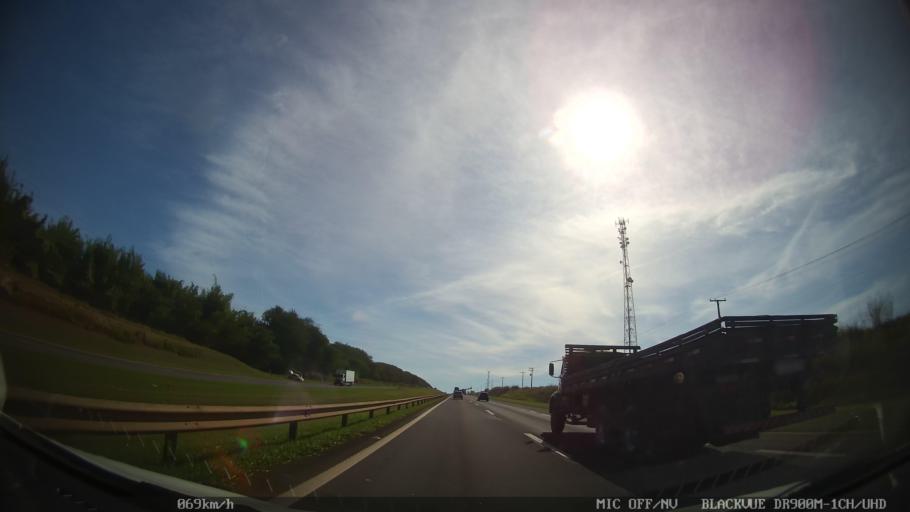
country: BR
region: Sao Paulo
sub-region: Leme
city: Leme
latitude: -22.2703
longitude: -47.3918
